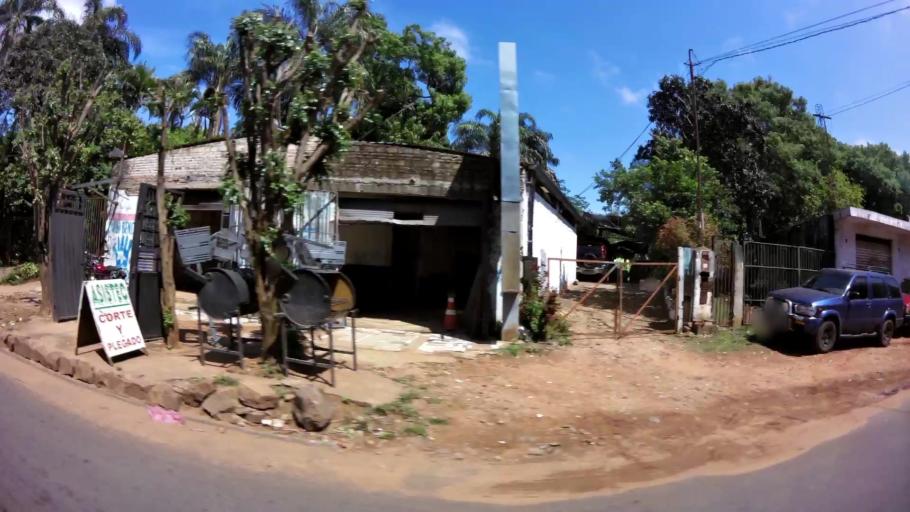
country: PY
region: Central
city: San Lorenzo
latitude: -25.3268
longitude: -57.5095
